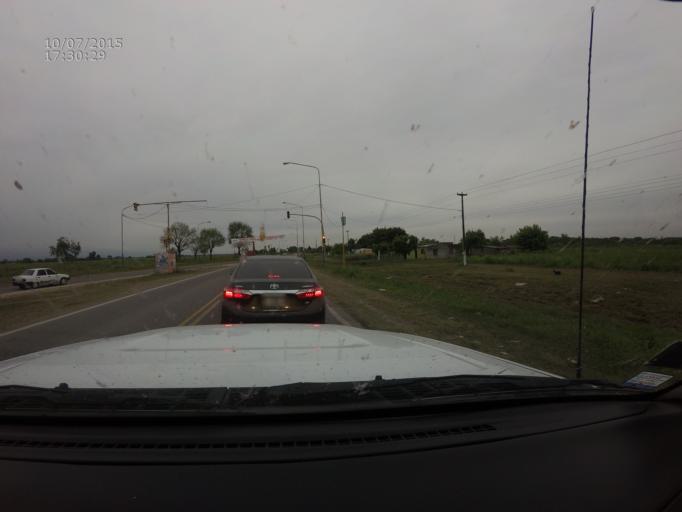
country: AR
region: Tucuman
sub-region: Departamento de Leales
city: Bella Vista
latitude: -27.0104
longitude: -65.2941
